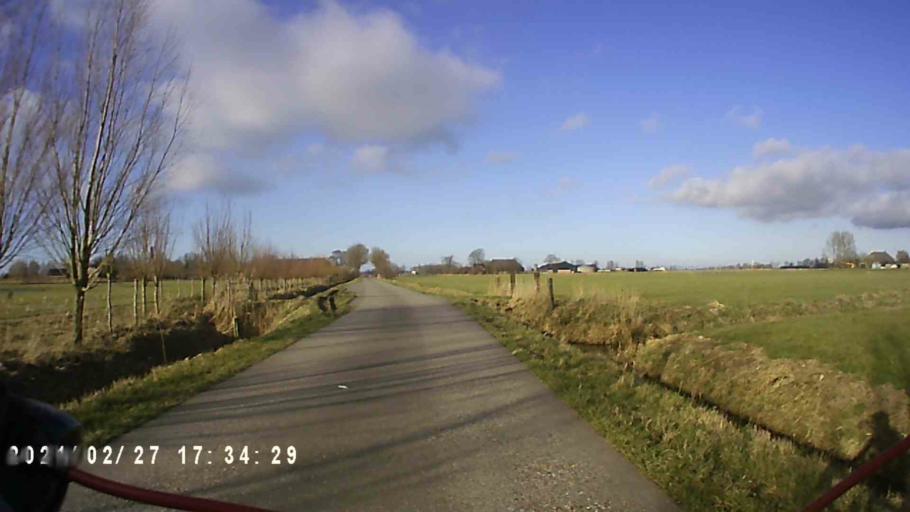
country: NL
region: Groningen
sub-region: Gemeente Bedum
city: Bedum
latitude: 53.3323
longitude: 6.5696
